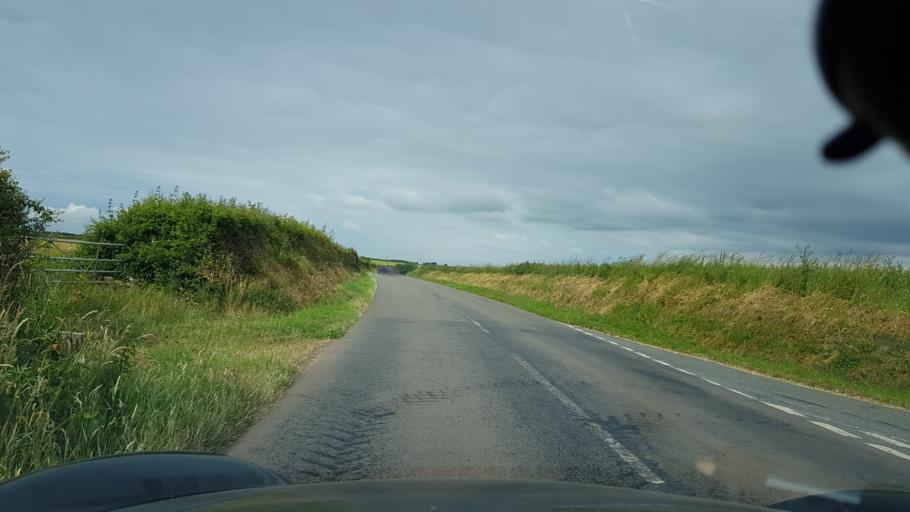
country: GB
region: Wales
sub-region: Pembrokeshire
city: Dale
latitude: 51.7461
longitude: -5.1456
